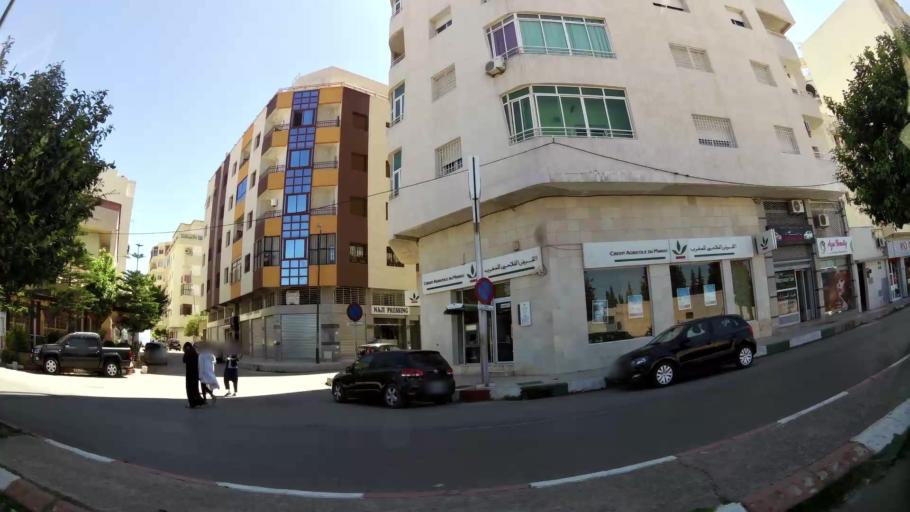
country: MA
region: Meknes-Tafilalet
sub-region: Meknes
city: Meknes
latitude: 33.9055
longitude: -5.5324
